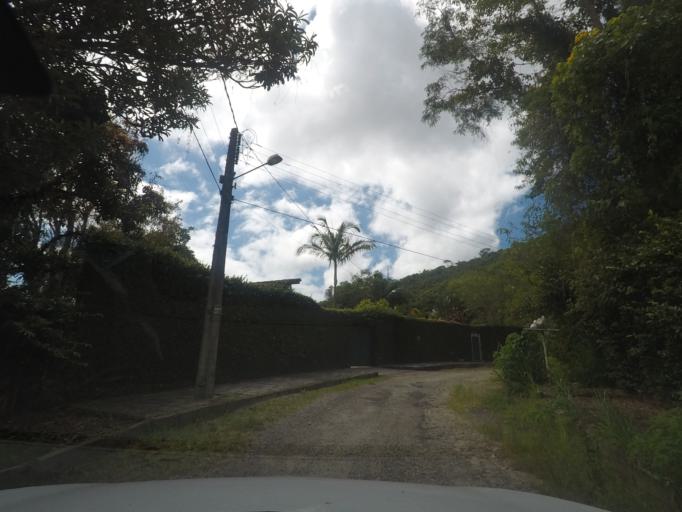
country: BR
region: Rio de Janeiro
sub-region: Teresopolis
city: Teresopolis
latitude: -22.3993
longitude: -42.9844
